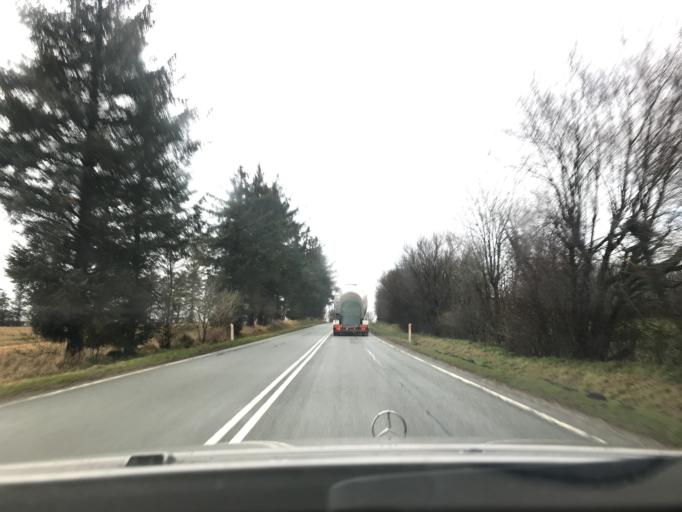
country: DK
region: South Denmark
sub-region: Esbjerg Kommune
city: Ribe
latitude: 55.2715
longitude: 8.8712
